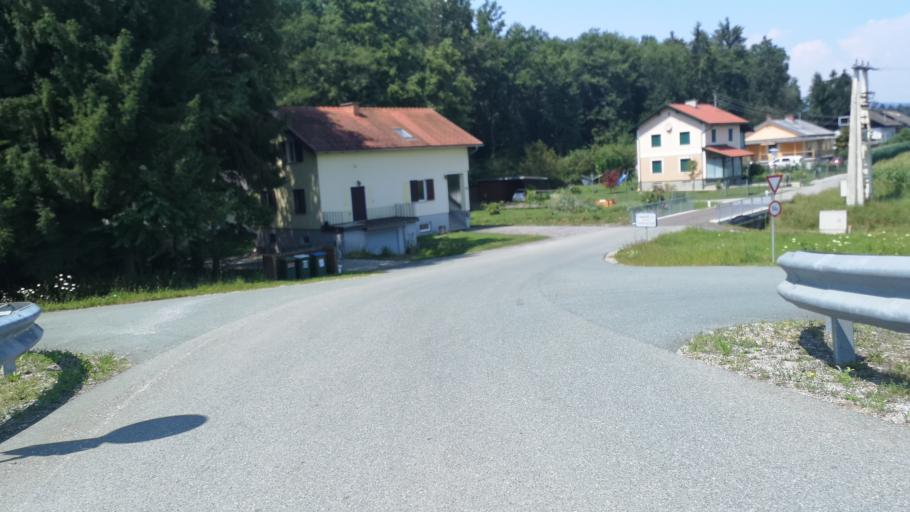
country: AT
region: Styria
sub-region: Politischer Bezirk Deutschlandsberg
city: Unterbergla
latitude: 46.8131
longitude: 15.2713
